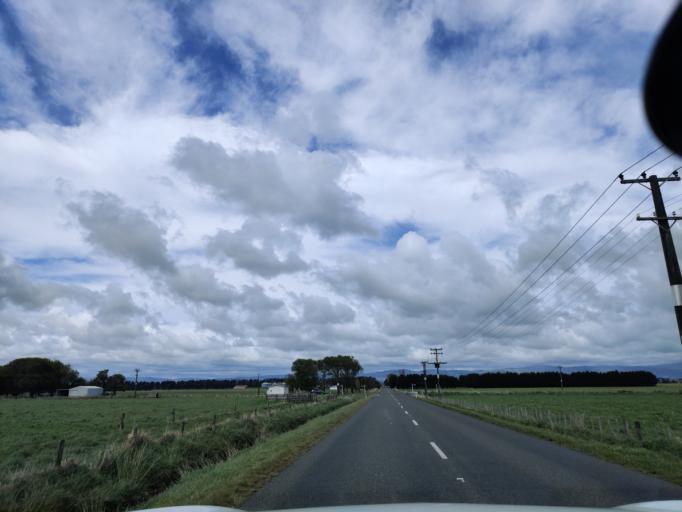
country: NZ
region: Manawatu-Wanganui
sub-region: Palmerston North City
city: Palmerston North
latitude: -40.3334
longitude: 175.5146
